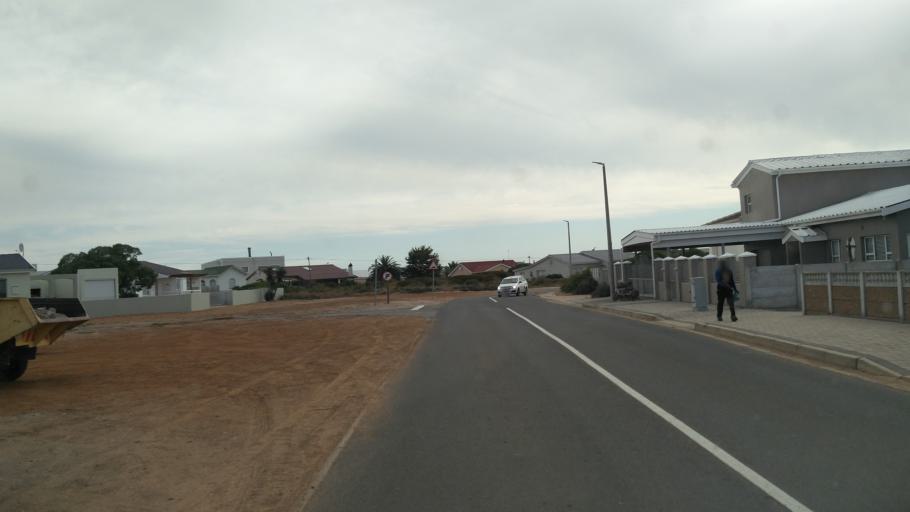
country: ZA
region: Western Cape
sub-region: City of Cape Town
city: Atlantis
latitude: -33.3459
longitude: 18.1610
